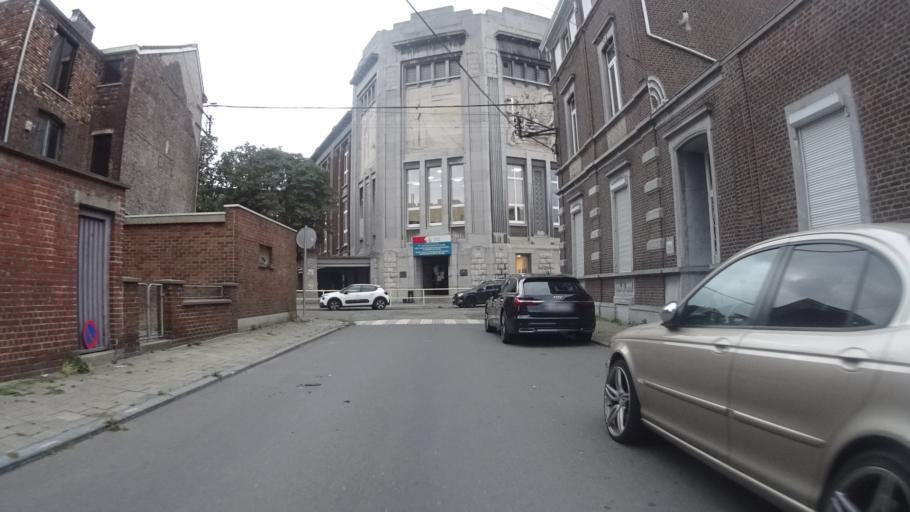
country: BE
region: Wallonia
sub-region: Province de Liege
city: Saint-Nicolas
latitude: 50.6133
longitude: 5.5078
